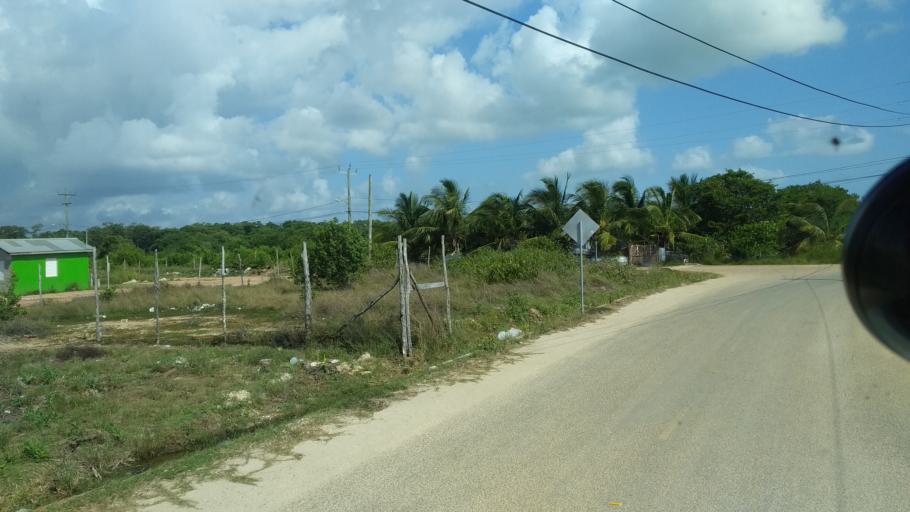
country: BZ
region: Belize
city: Belize City
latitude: 17.5162
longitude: -88.2345
